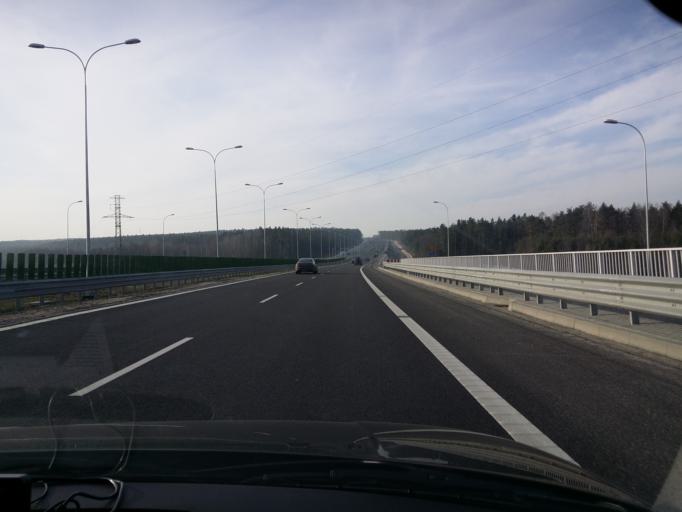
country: PL
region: Swietokrzyskie
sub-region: Powiat skarzyski
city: Skarzysko-Kamienna
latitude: 51.1578
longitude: 20.8520
